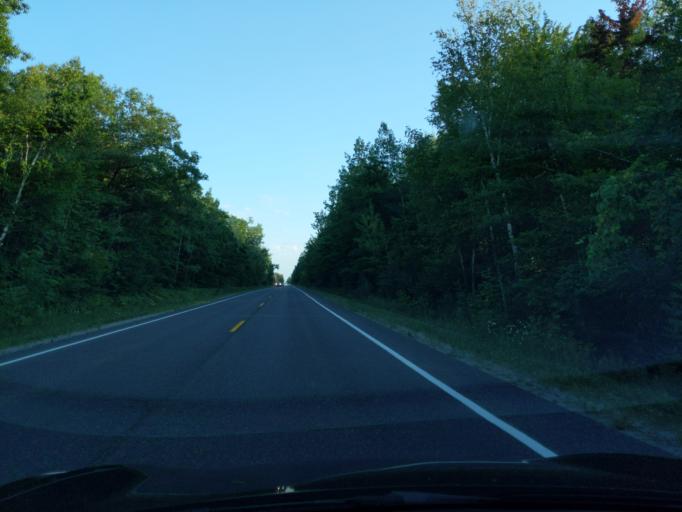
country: US
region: Michigan
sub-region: Midland County
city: Midland
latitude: 43.5295
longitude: -84.3698
